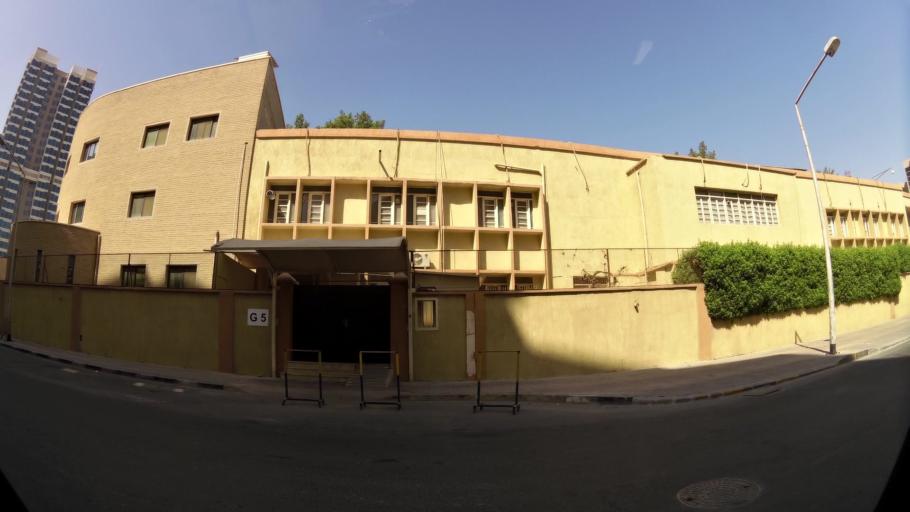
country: KW
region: Al Asimah
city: Kuwait City
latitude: 29.3875
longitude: 47.9926
